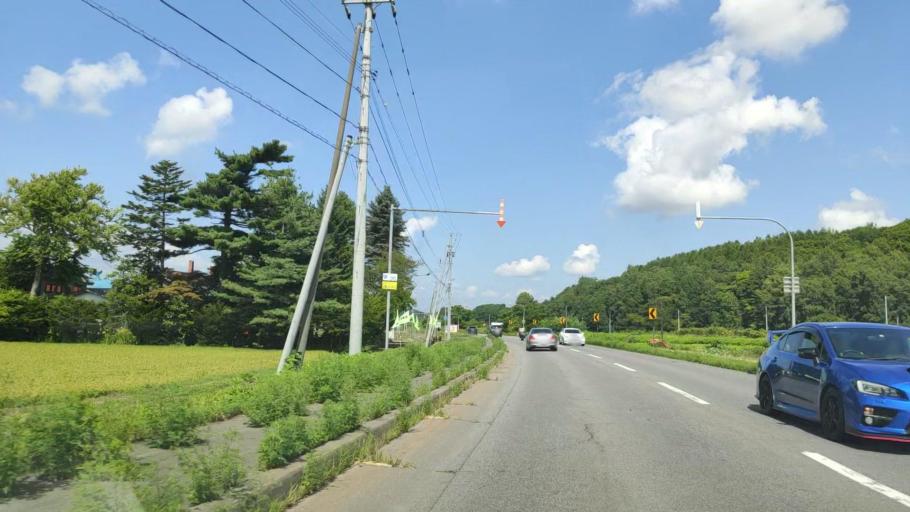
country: JP
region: Hokkaido
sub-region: Asahikawa-shi
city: Asahikawa
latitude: 43.6281
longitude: 142.4645
